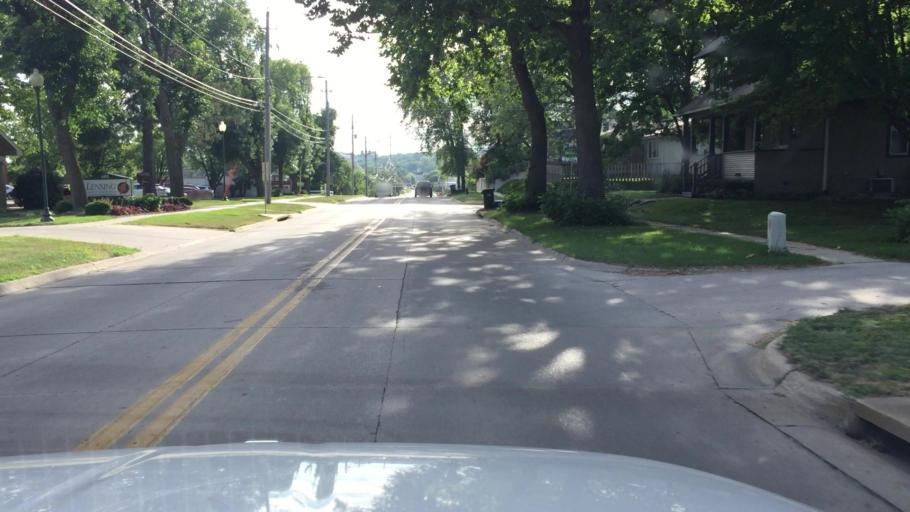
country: US
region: Iowa
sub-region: Johnson County
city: Iowa City
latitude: 41.6495
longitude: -91.5272
